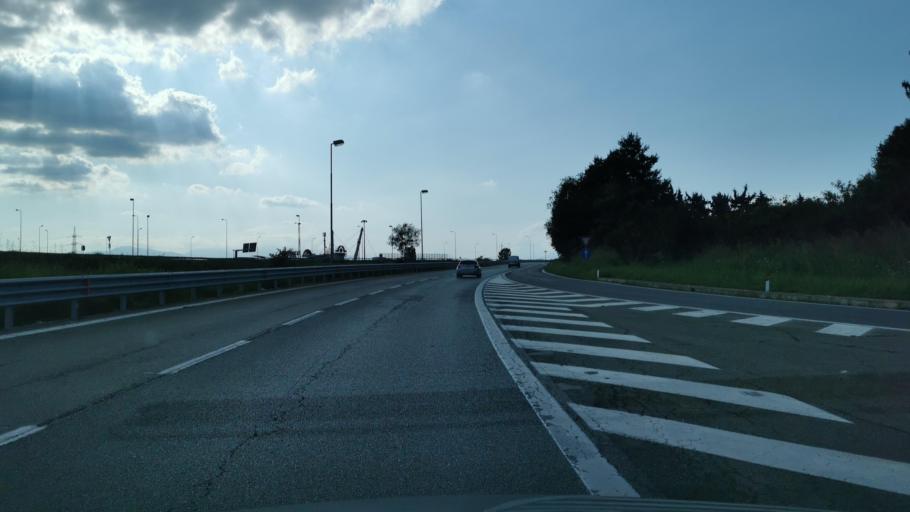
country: IT
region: Piedmont
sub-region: Provincia di Torino
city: Fornaci
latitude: 45.0244
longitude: 7.5988
